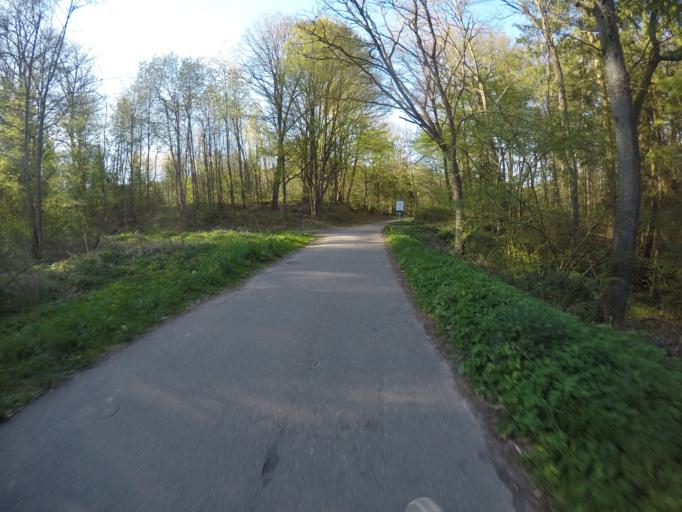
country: DE
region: Baden-Wuerttemberg
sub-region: Regierungsbezirk Stuttgart
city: Steinenbronn
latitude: 48.6756
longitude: 9.1259
